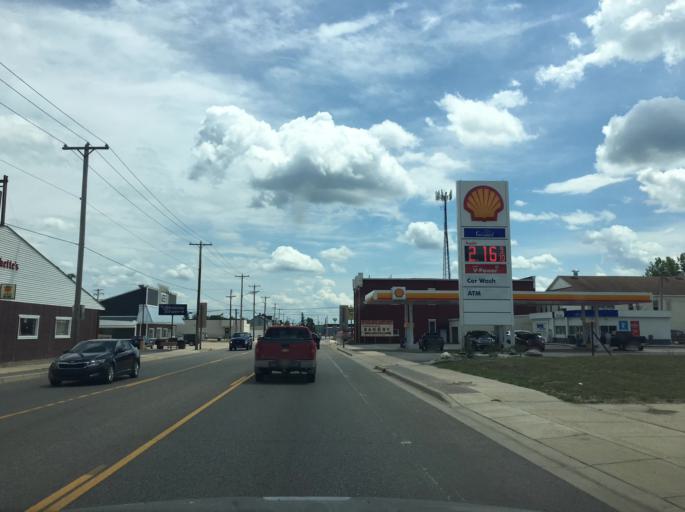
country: US
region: Michigan
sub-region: Crawford County
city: Grayling
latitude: 44.6630
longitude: -84.7169
